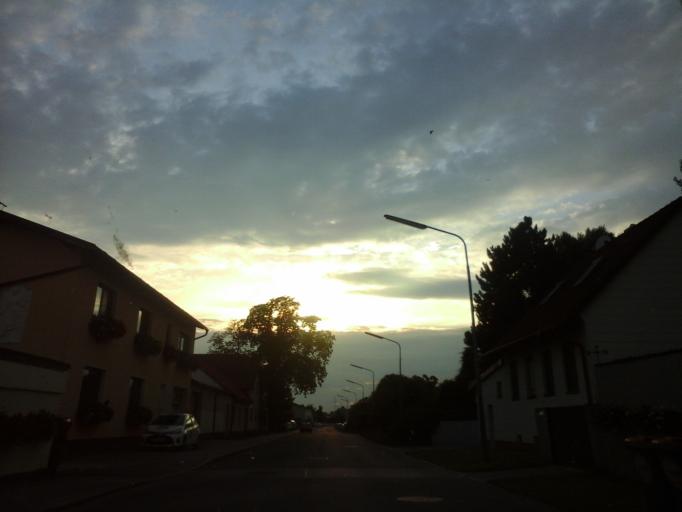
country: AT
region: Lower Austria
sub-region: Politischer Bezirk Wien-Umgebung
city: Schwechat
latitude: 48.1587
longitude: 16.4900
